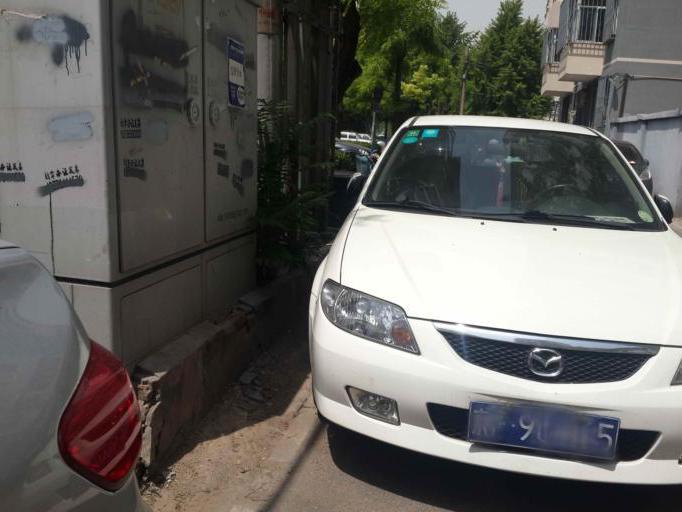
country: CN
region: Beijing
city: Chaowai
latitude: 39.9268
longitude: 116.4289
